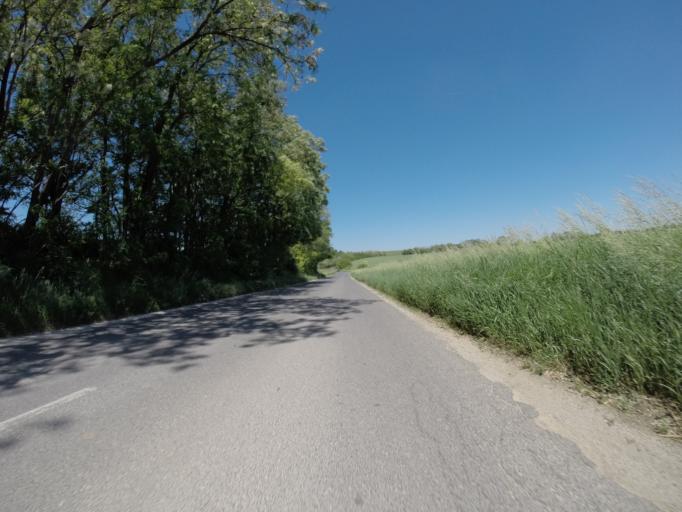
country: SK
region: Trnavsky
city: Hlohovec
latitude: 48.4696
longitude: 17.8562
